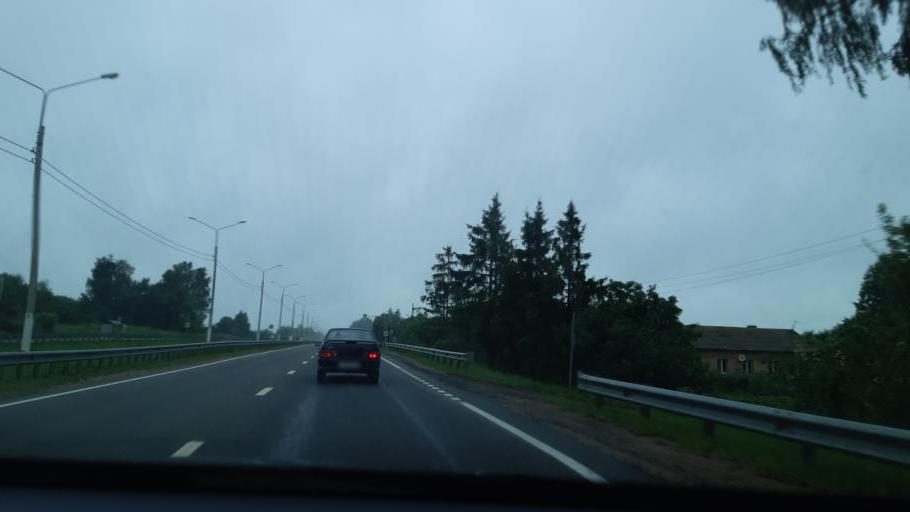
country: RU
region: Smolensk
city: Talashkino
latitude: 54.6723
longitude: 32.1483
